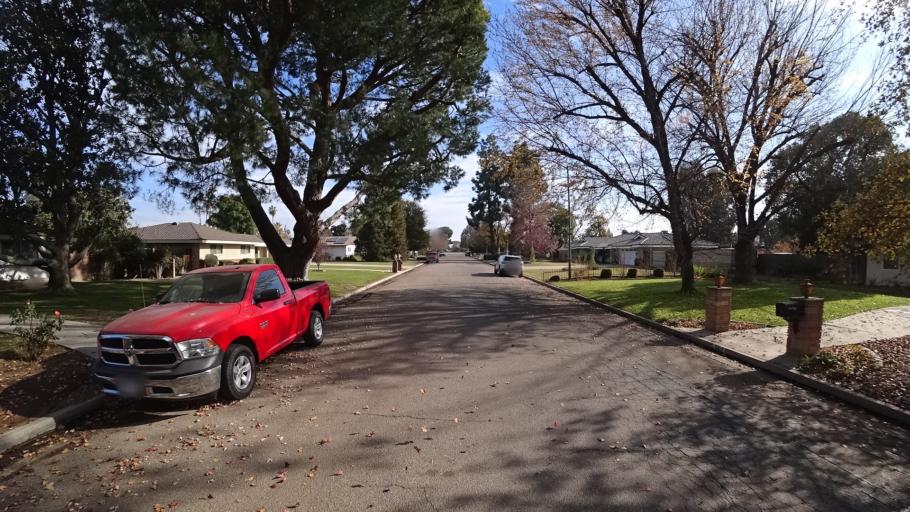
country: US
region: California
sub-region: Kern County
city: Greenacres
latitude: 35.4113
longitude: -119.0691
